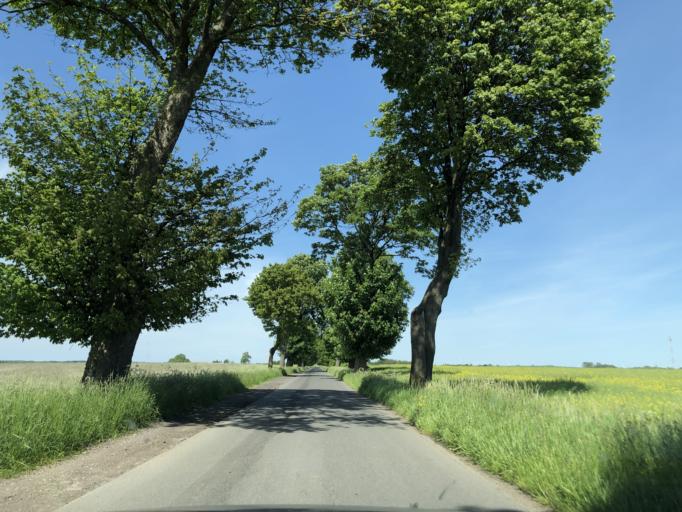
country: PL
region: West Pomeranian Voivodeship
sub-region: Powiat kolobrzeski
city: Dygowo
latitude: 54.1173
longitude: 15.7072
